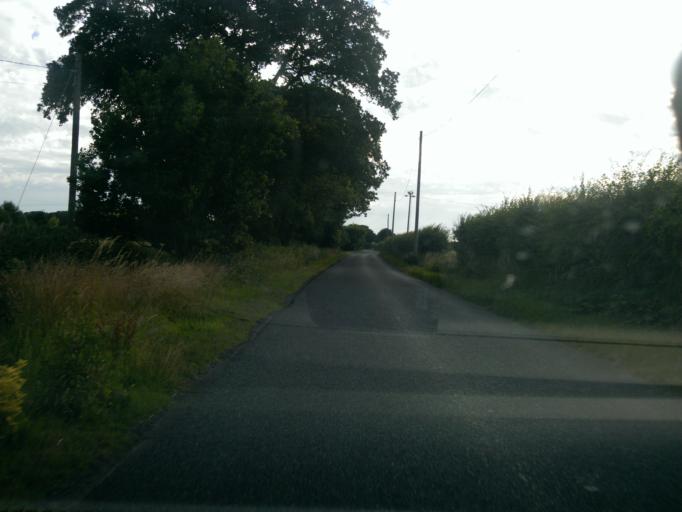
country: GB
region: England
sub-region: Essex
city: Great Bentley
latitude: 51.8403
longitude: 1.1015
